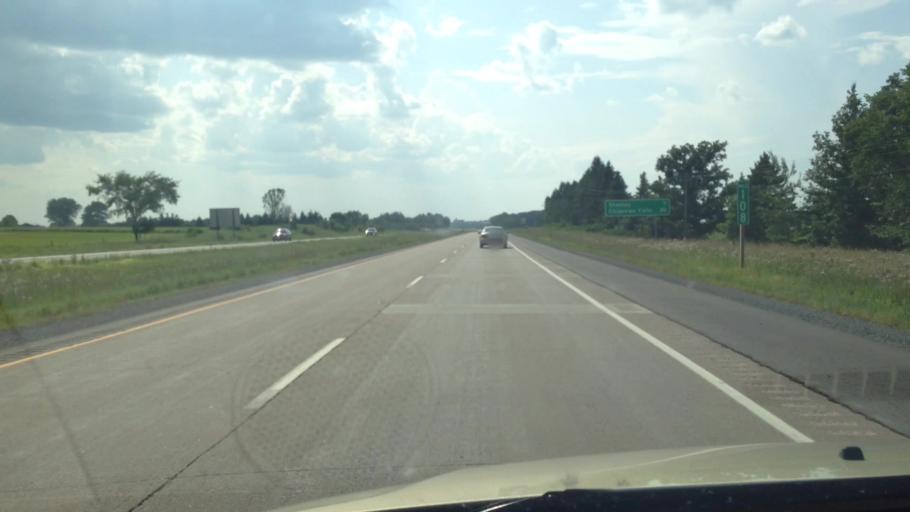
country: US
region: Wisconsin
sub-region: Clark County
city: Thorp
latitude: 44.9516
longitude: -90.8130
